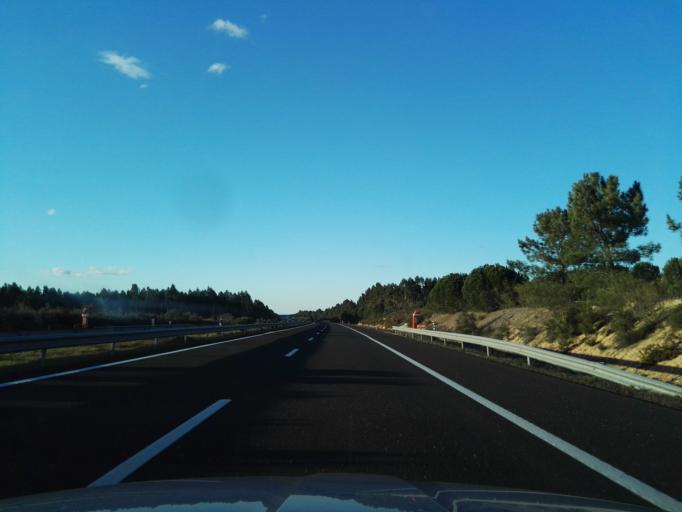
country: PT
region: Santarem
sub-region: Benavente
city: Poceirao
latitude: 38.7886
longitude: -8.6884
